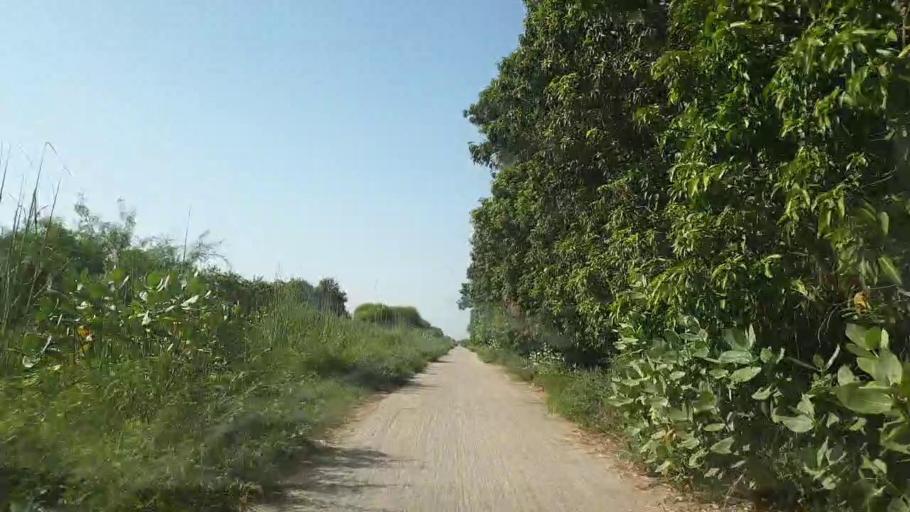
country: PK
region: Sindh
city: Tando Jam
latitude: 25.3308
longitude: 68.5898
